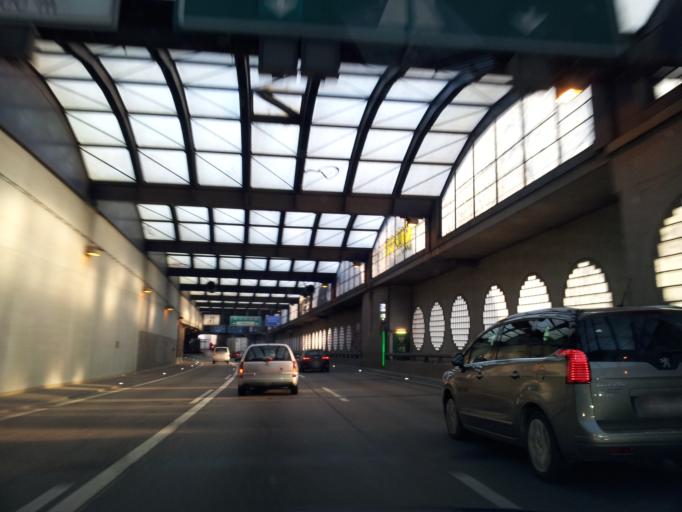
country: CH
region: Basel-Landschaft
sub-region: Bezirk Arlesheim
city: Birsfelden
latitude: 47.5516
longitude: 7.6165
